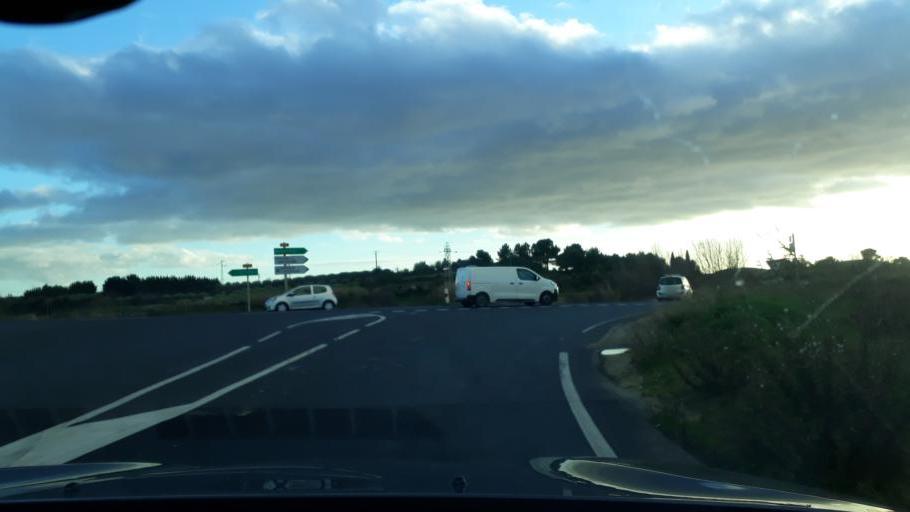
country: FR
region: Languedoc-Roussillon
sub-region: Departement de l'Herault
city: Nissan-lez-Enserune
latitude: 43.2948
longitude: 3.1315
